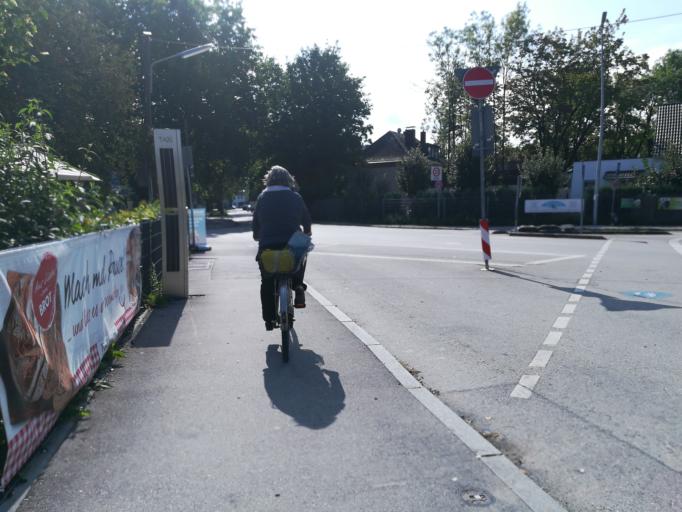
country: DE
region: Bavaria
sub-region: Upper Bavaria
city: Karlsfeld
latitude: 48.1967
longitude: 11.5249
